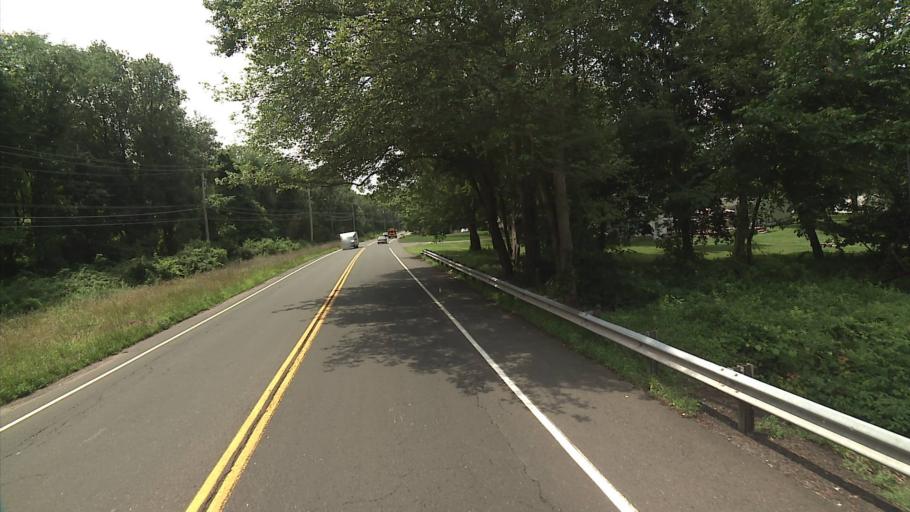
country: US
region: Connecticut
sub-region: New Haven County
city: North Haven
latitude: 41.3477
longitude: -72.8546
